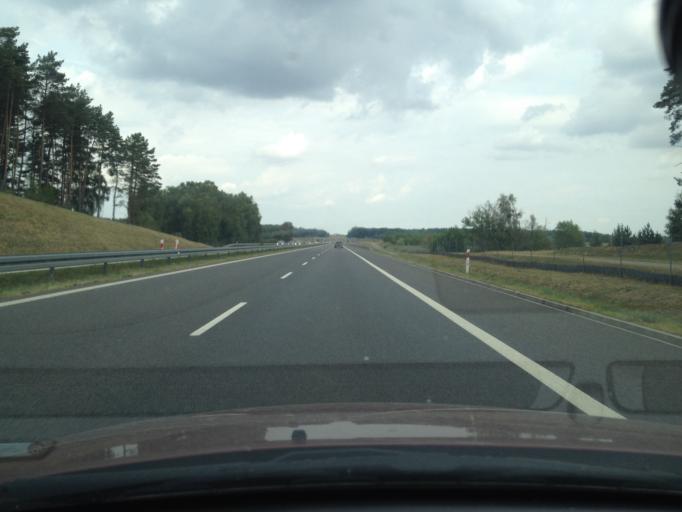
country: PL
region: West Pomeranian Voivodeship
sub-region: Powiat mysliborski
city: Mysliborz
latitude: 52.9990
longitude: 14.8622
